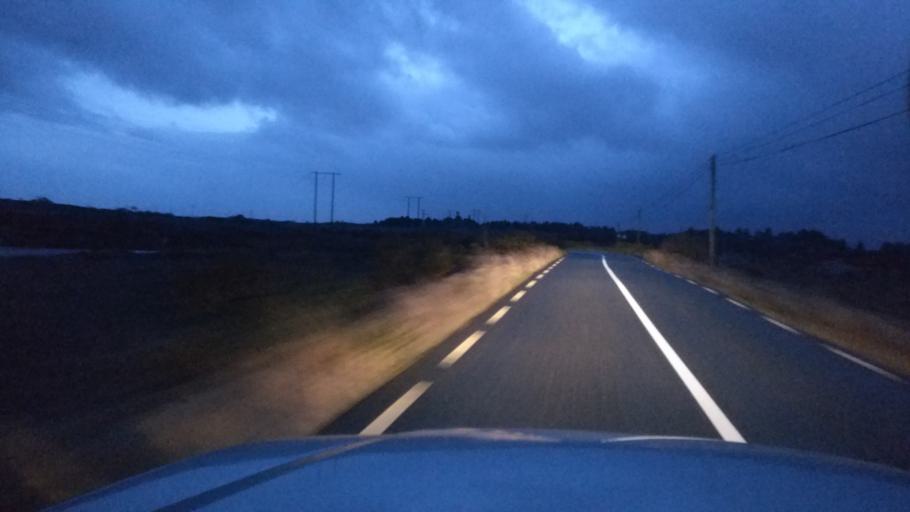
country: IE
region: Connaught
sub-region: County Galway
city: Oughterard
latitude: 53.3963
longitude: -9.5469
